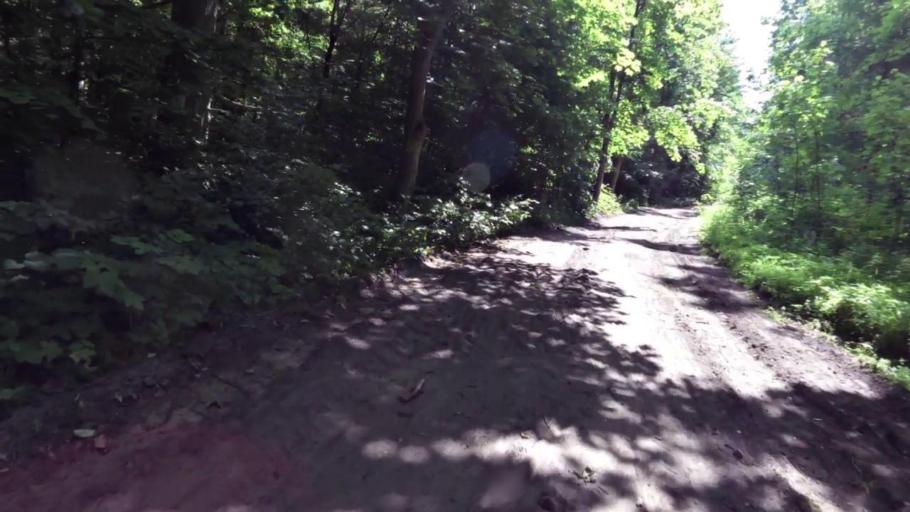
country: PL
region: West Pomeranian Voivodeship
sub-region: Powiat kamienski
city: Miedzyzdroje
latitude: 53.9324
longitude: 14.5309
